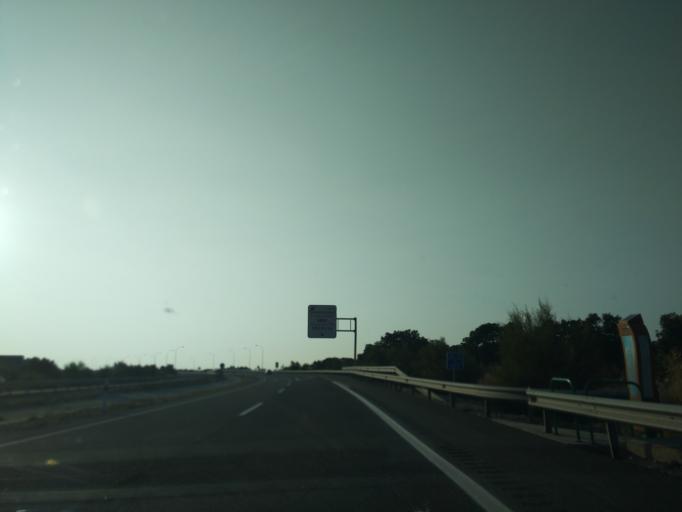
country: ES
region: Castille and Leon
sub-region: Provincia de Avila
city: Berrocalejo de Aragona
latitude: 40.6772
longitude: -4.6271
